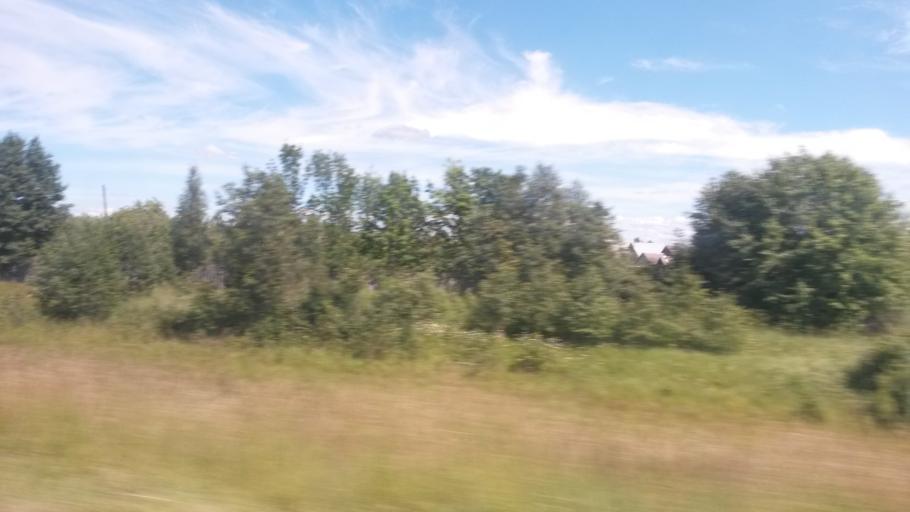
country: RU
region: Ivanovo
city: Staraya Vichuga
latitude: 57.2245
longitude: 41.8627
